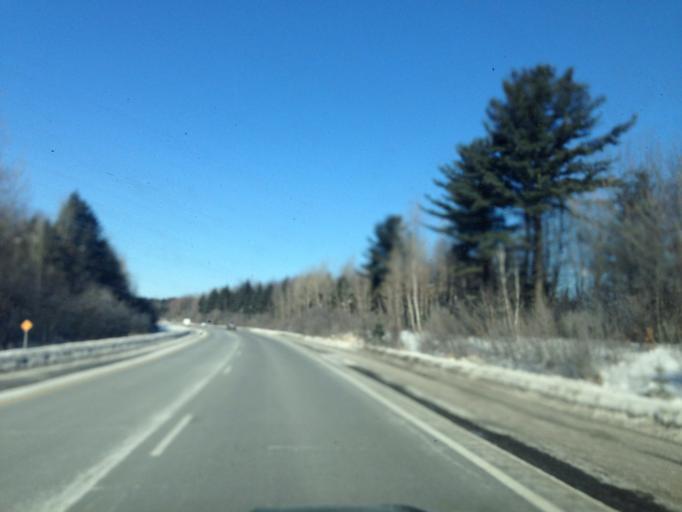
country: CA
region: Ontario
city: Ottawa
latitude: 45.3615
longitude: -75.4789
